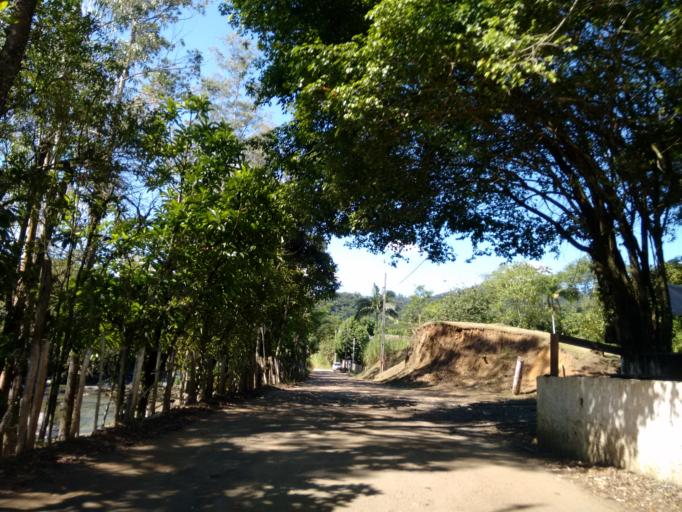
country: BR
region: Santa Catarina
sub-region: Indaial
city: Indaial
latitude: -26.9015
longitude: -49.1906
